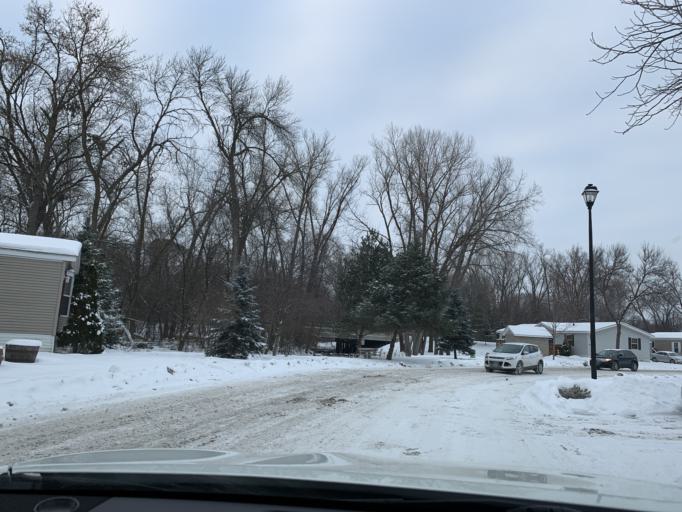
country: US
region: Minnesota
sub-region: Anoka County
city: Coon Rapids
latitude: 45.1606
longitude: -93.2961
